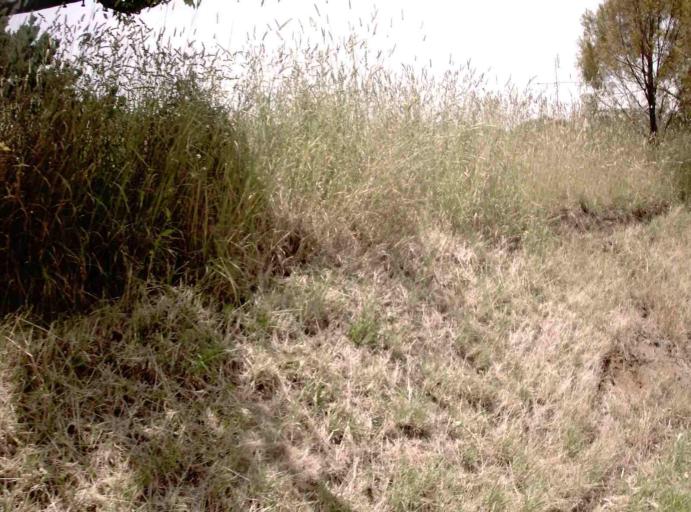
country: AU
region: Victoria
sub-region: Latrobe
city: Traralgon
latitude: -38.3271
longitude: 146.7237
